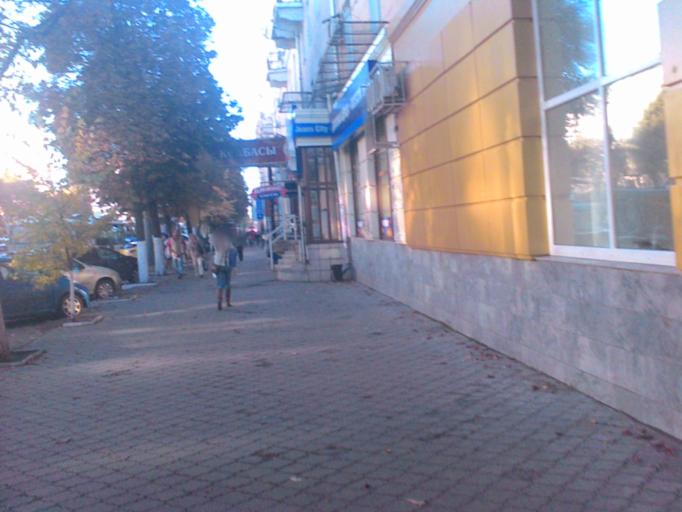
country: RU
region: Voronezj
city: Voronezh
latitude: 51.6698
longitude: 39.1899
